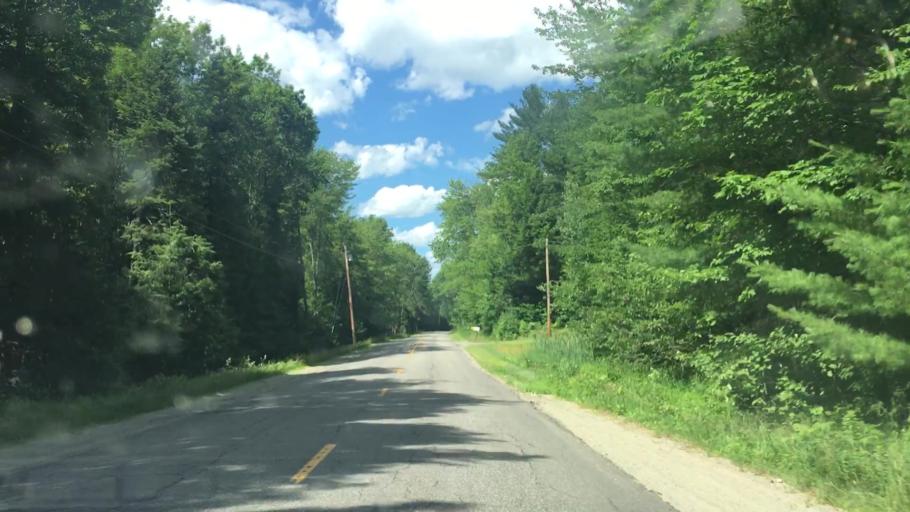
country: US
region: Maine
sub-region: Franklin County
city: Chesterville
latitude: 44.6077
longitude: -70.0830
